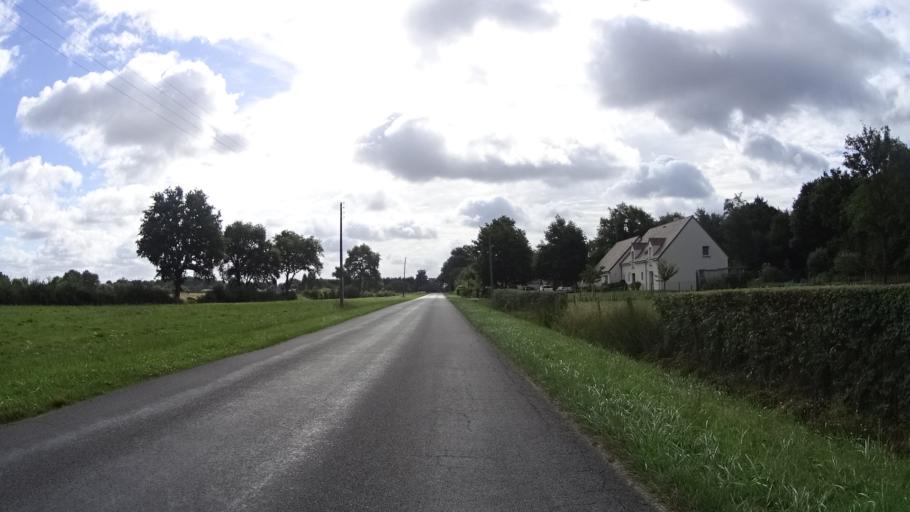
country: FR
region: Centre
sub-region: Departement du Loiret
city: Lorris
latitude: 47.8913
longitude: 2.4937
